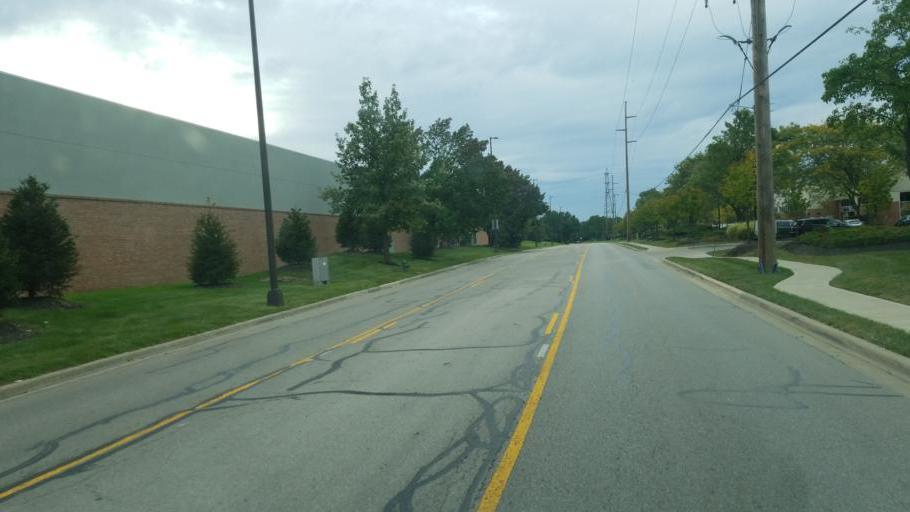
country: US
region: Ohio
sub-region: Franklin County
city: Dublin
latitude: 40.1077
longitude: -83.0933
